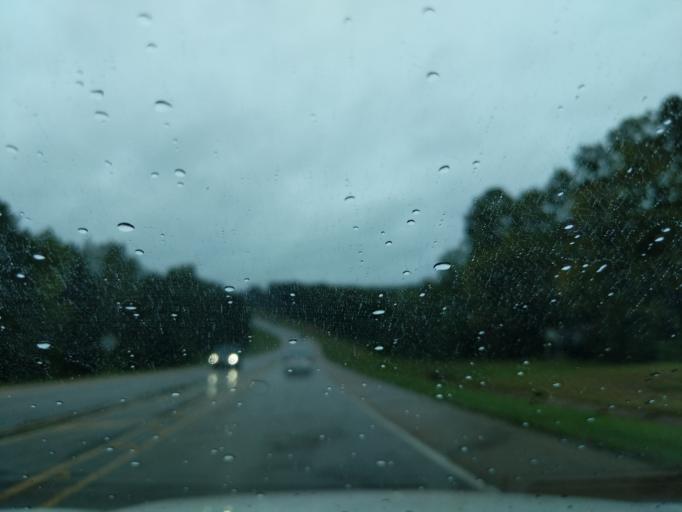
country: US
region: Louisiana
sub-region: Webster Parish
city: Minden
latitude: 32.6004
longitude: -93.2499
